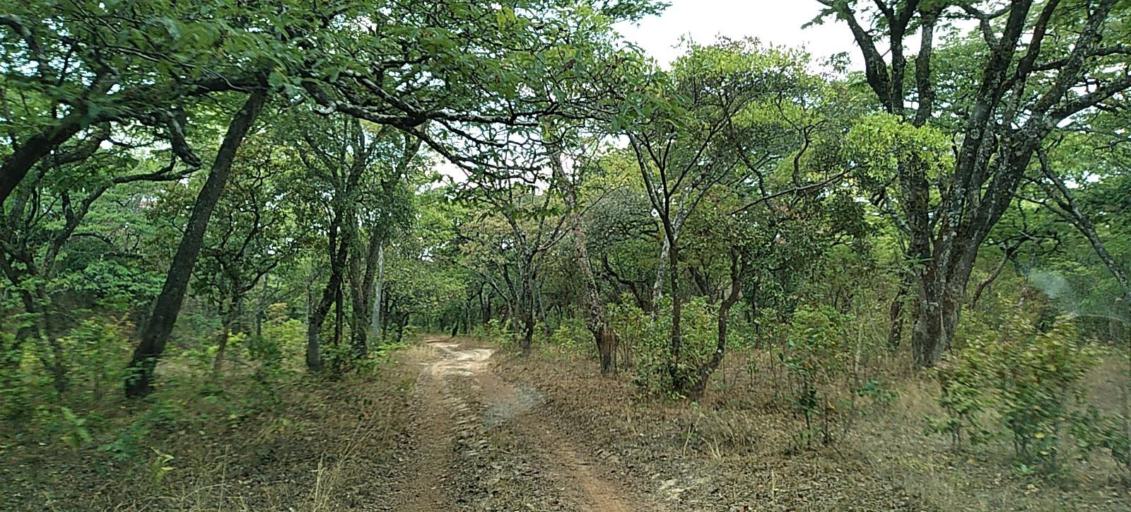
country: ZM
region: Copperbelt
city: Chililabombwe
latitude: -12.4761
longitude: 27.7006
